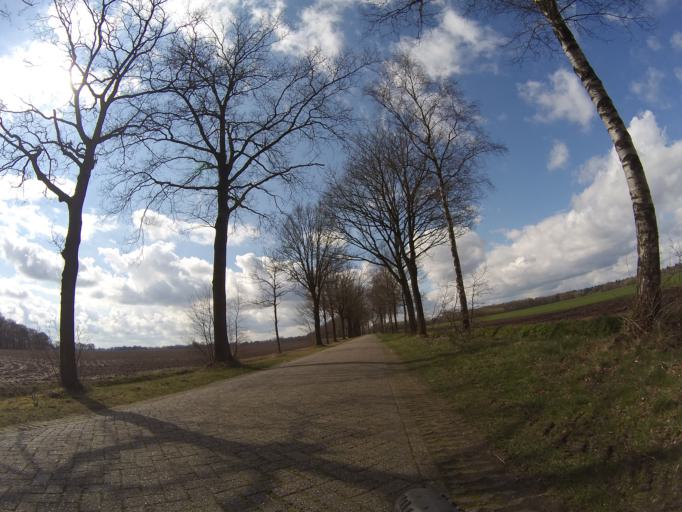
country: NL
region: Drenthe
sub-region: Gemeente Coevorden
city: Dalen
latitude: 52.7475
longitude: 6.6789
